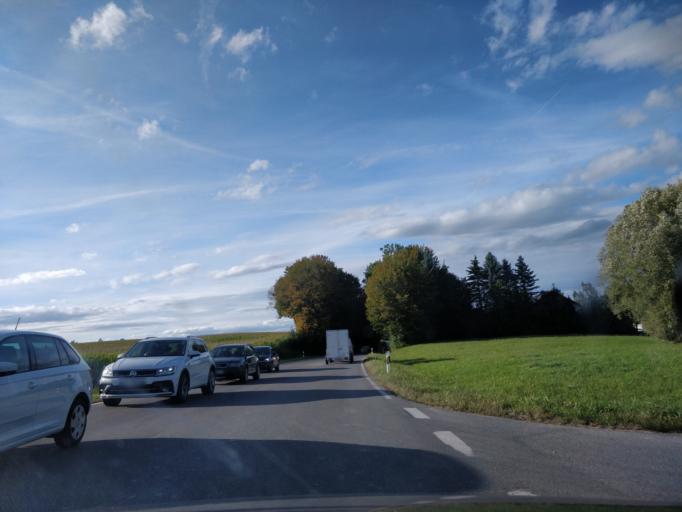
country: DE
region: Bavaria
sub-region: Swabia
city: Friedberg
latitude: 48.3421
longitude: 10.9968
